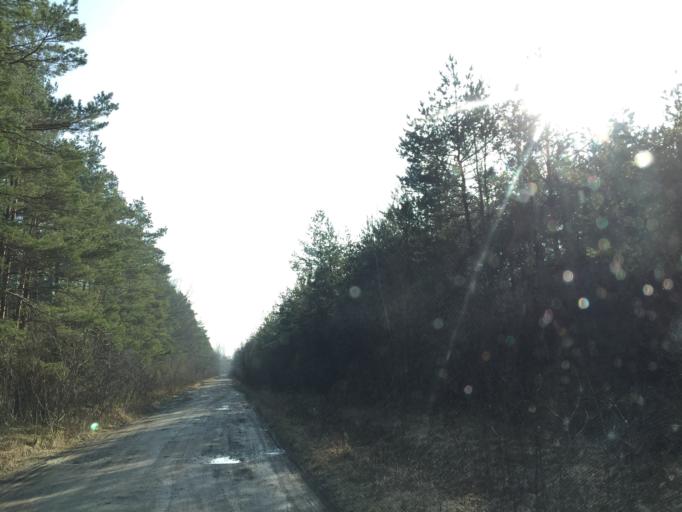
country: EE
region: Saare
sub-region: Kuressaare linn
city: Kuressaare
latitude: 58.2382
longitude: 22.4475
